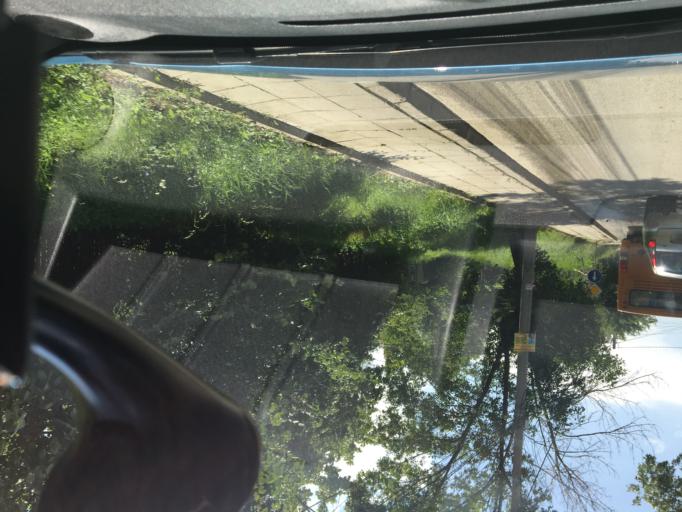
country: BG
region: Sofia-Capital
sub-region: Stolichna Obshtina
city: Sofia
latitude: 42.6205
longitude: 23.3345
